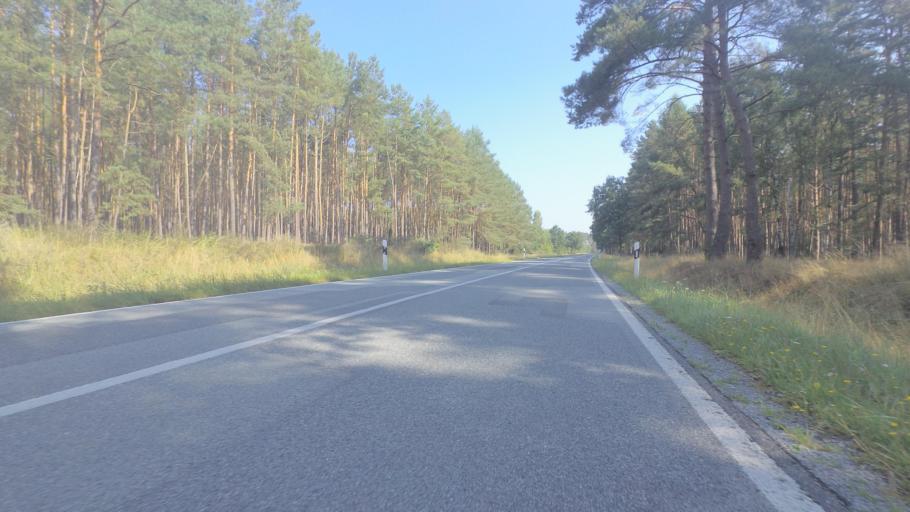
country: DE
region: Mecklenburg-Vorpommern
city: Malchow
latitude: 53.5686
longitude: 12.4542
